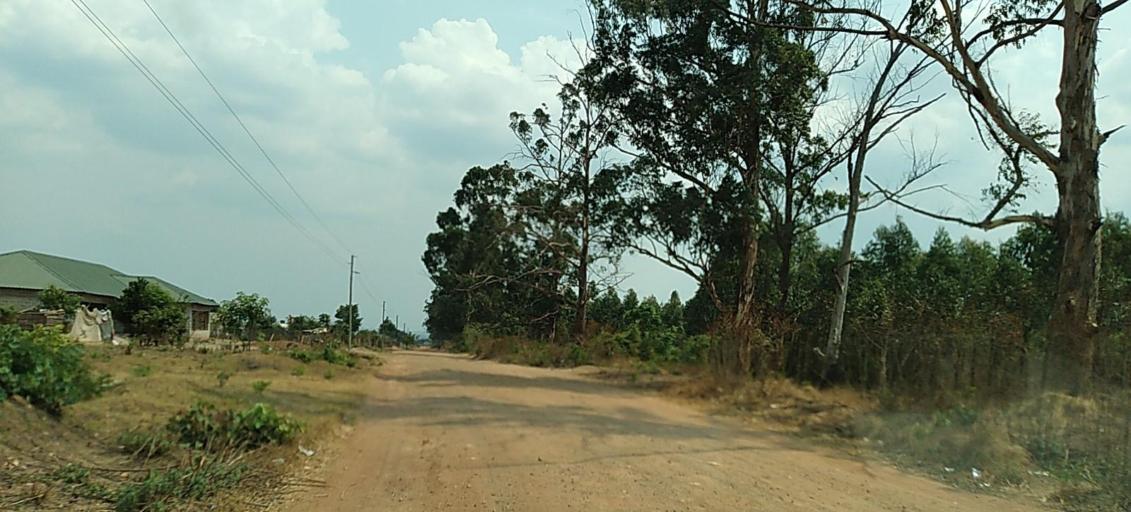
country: ZM
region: Copperbelt
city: Kalulushi
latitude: -12.8454
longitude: 28.0779
